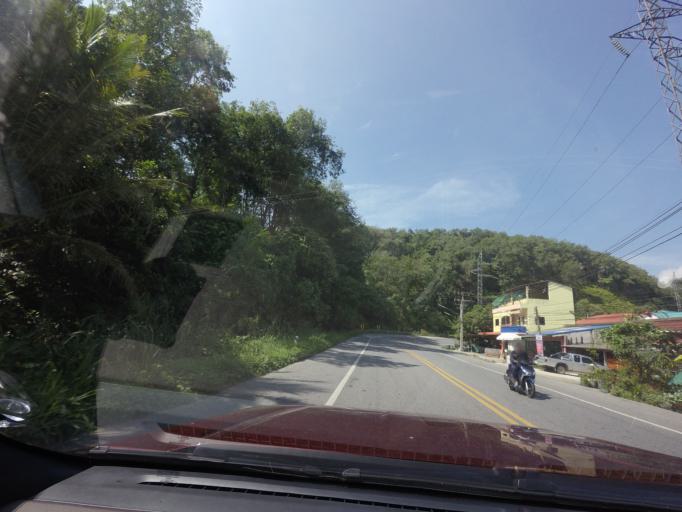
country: TH
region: Yala
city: Betong
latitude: 5.8611
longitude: 101.1261
